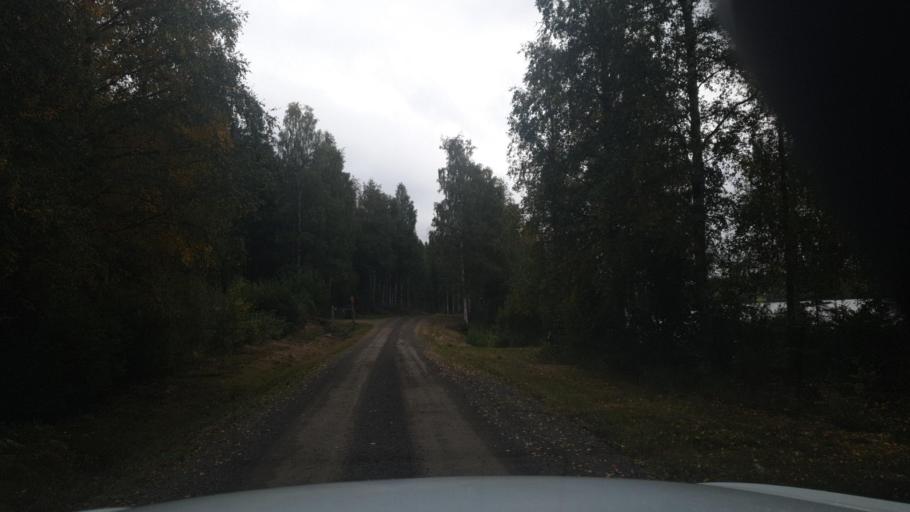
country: SE
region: Vaermland
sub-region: Arvika Kommun
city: Arvika
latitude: 59.8682
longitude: 12.8093
